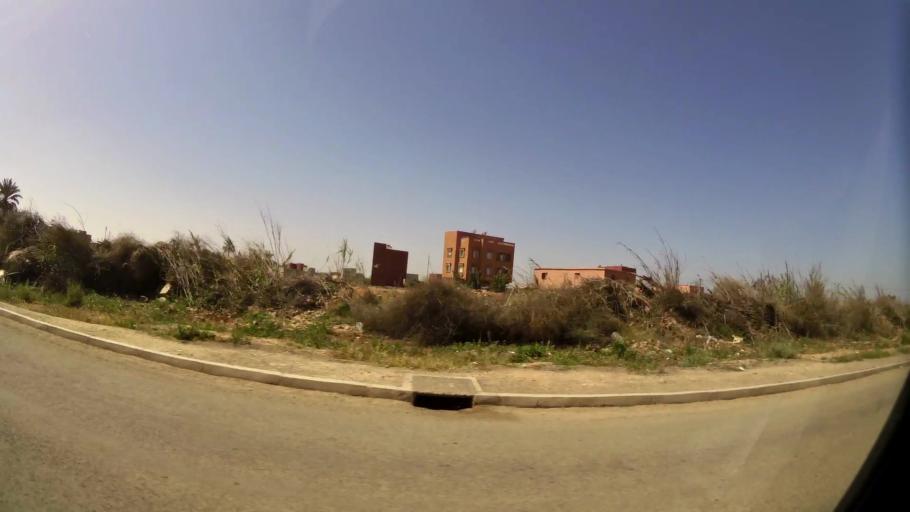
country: MA
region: Souss-Massa-Draa
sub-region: Inezgane-Ait Mellou
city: Inezgane
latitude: 30.3276
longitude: -9.5088
